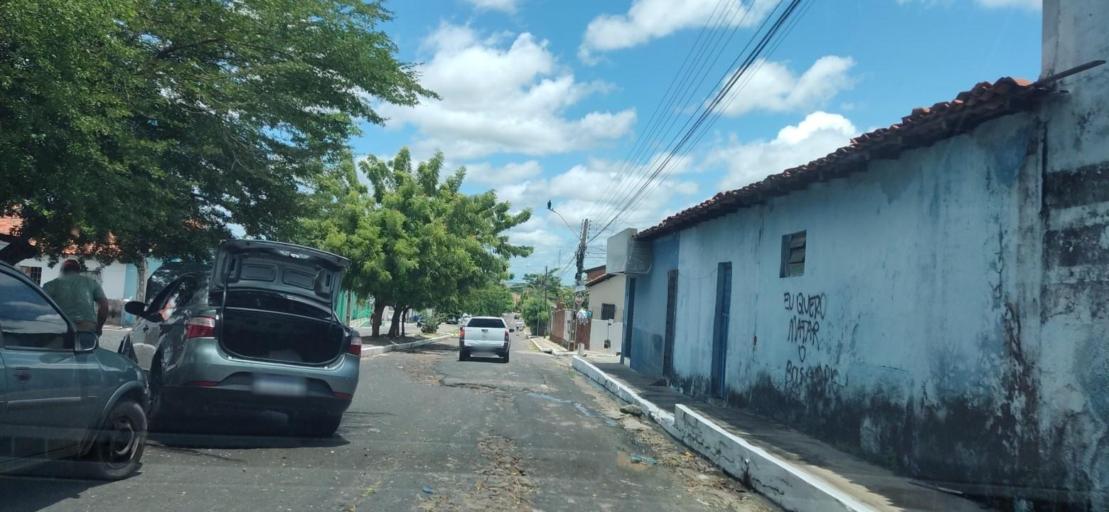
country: BR
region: Piaui
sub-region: Teresina
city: Teresina
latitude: -5.1458
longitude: -42.7817
